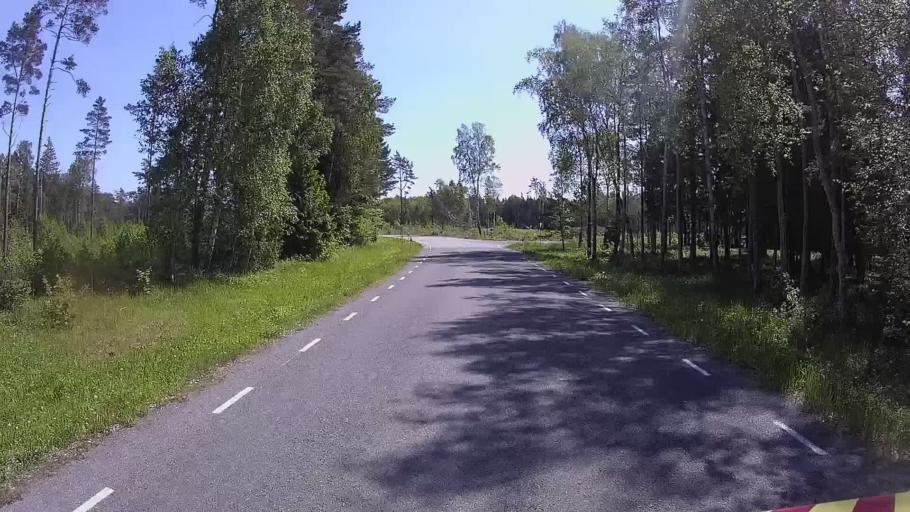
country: EE
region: Saare
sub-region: Kuressaare linn
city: Kuressaare
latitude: 57.9626
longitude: 22.1058
